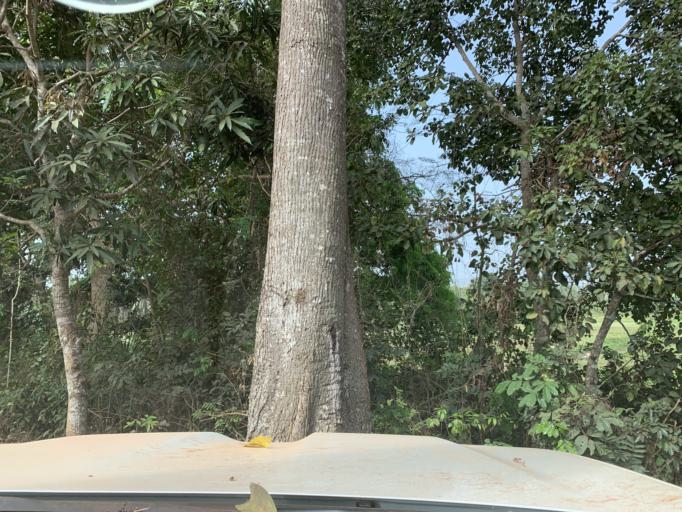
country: GN
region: Kindia
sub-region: Kindia
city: Kindia
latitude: 9.9756
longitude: -12.9836
